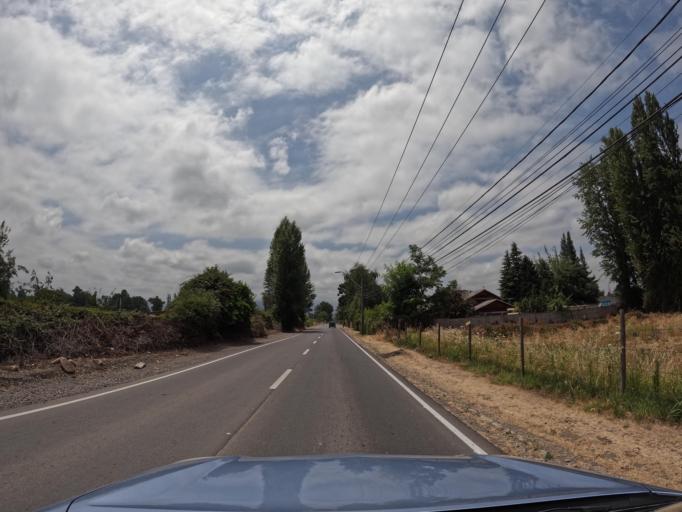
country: CL
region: O'Higgins
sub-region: Provincia de Colchagua
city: Chimbarongo
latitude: -34.7299
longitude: -70.9930
